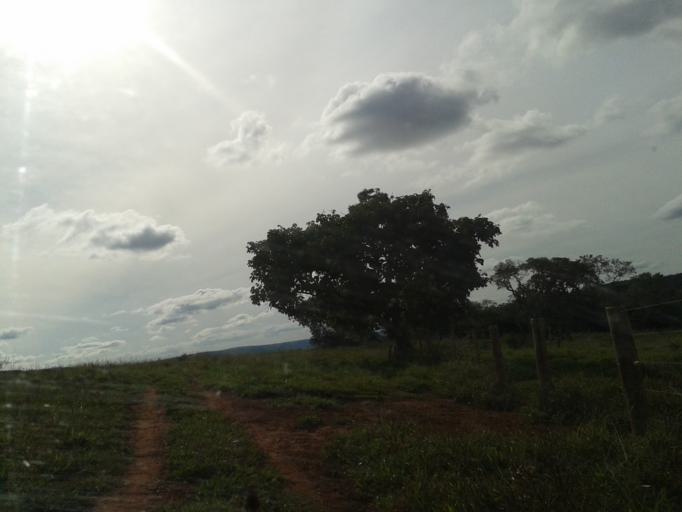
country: BR
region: Minas Gerais
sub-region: Campina Verde
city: Campina Verde
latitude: -19.4304
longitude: -49.7249
